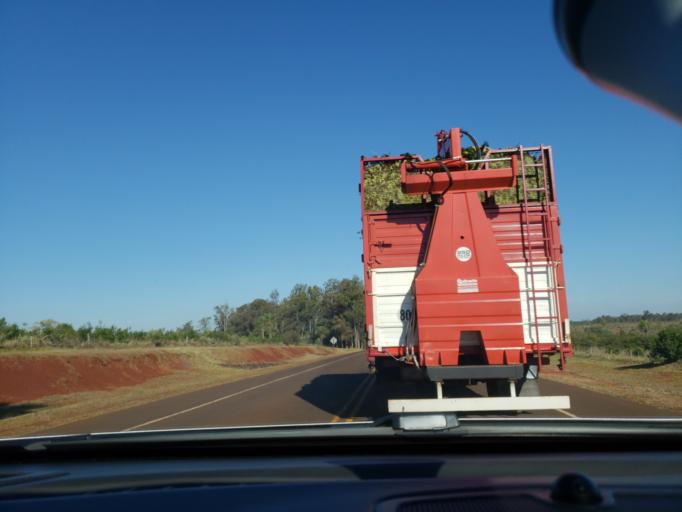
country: AR
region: Misiones
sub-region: Departamento de Apostoles
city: San Jose
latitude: -27.8320
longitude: -55.7697
